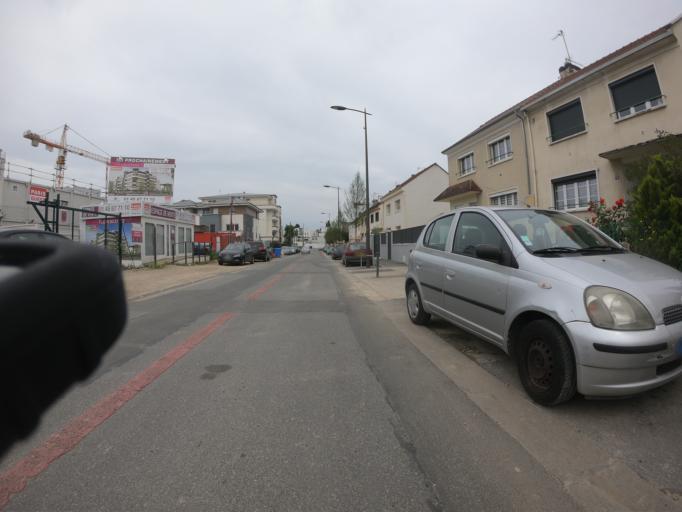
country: FR
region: Ile-de-France
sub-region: Departement du Val-de-Marne
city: Thiais
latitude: 48.7645
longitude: 2.3838
